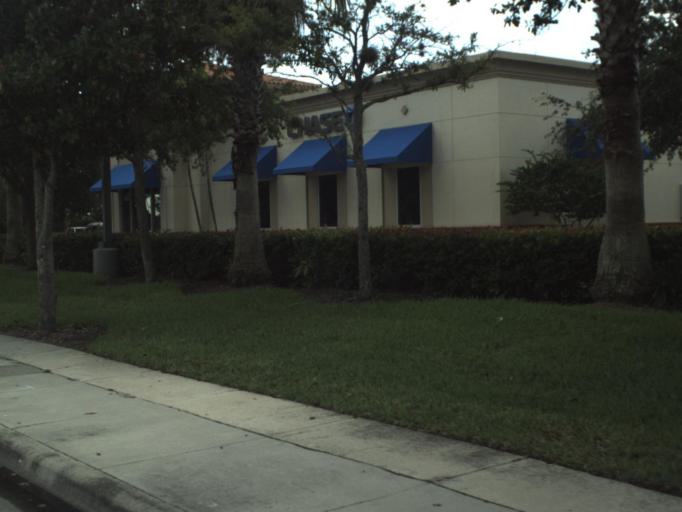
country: US
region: Florida
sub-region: Palm Beach County
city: Lake Park
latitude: 26.8073
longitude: -80.0598
